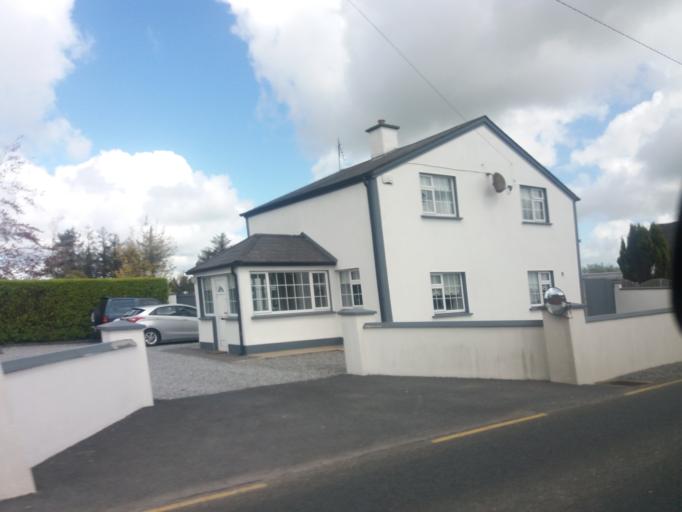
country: IE
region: Leinster
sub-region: Loch Garman
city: Loch Garman
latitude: 52.3200
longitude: -6.5141
